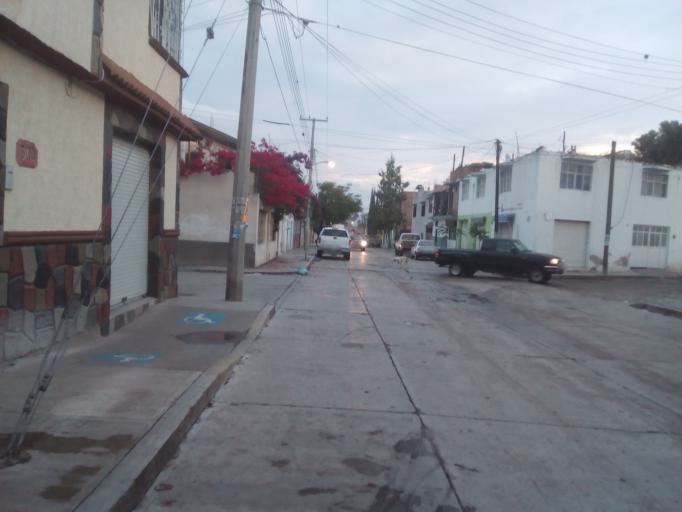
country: MX
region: Guerrero
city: San Luis de la Paz
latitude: 21.2924
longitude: -100.5247
